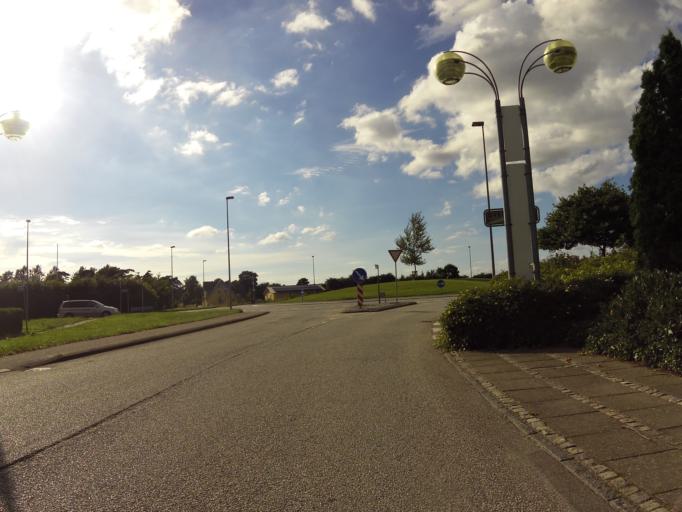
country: DK
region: South Denmark
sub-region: Haderslev Kommune
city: Vojens
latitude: 55.1976
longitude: 9.2967
